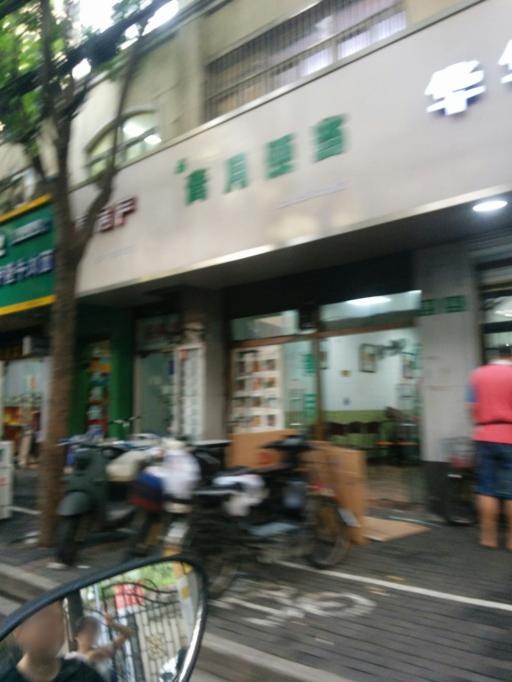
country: CN
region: Shanghai Shi
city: Shanghai
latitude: 31.2336
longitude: 121.4566
